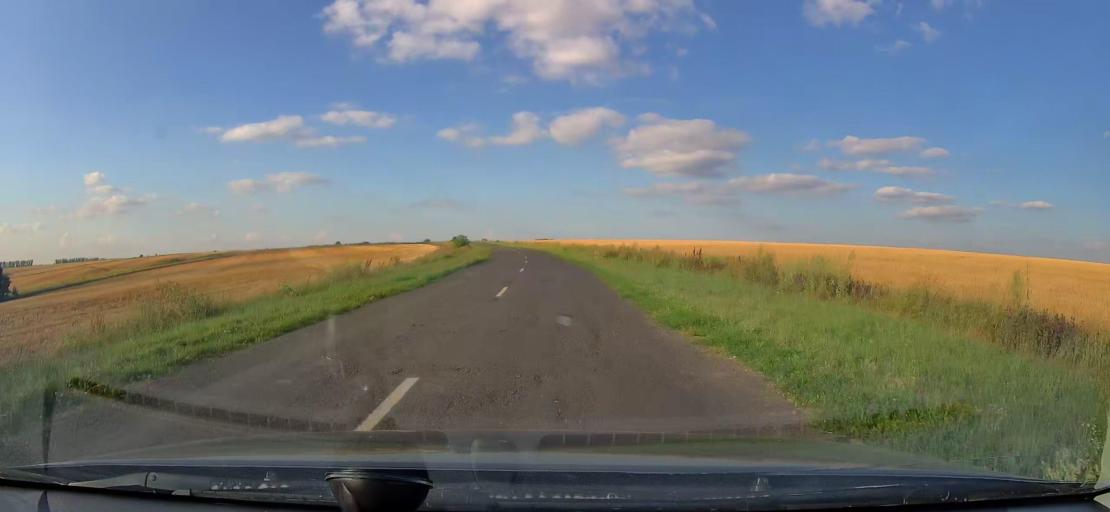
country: RU
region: Kursk
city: Zolotukhino
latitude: 52.0300
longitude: 36.2158
